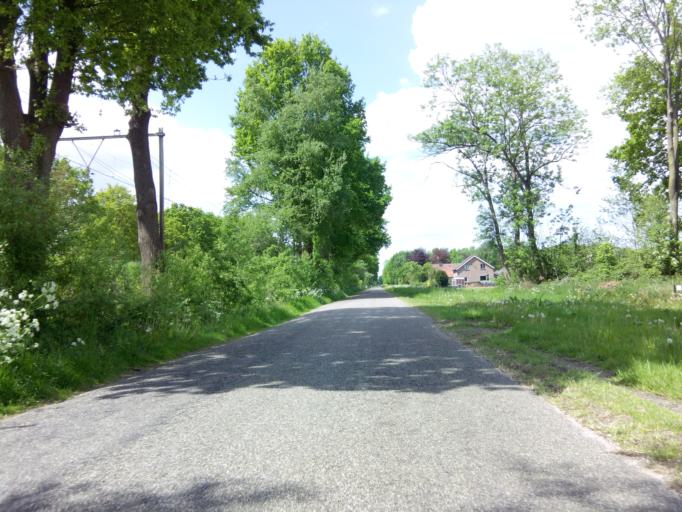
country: NL
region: Utrecht
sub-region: Gemeente Utrechtse Heuvelrug
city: Overberg
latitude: 52.0505
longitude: 5.5203
